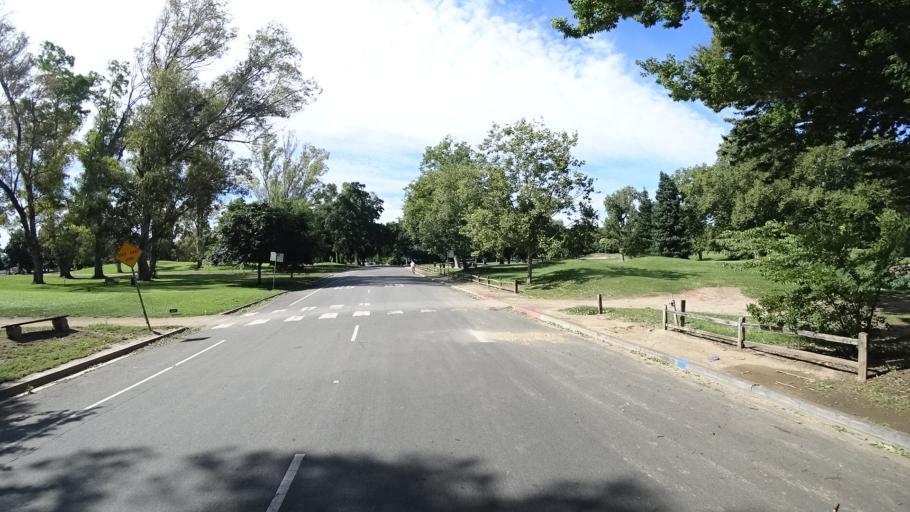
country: US
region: California
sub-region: Sacramento County
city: Sacramento
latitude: 38.5414
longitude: -121.4973
